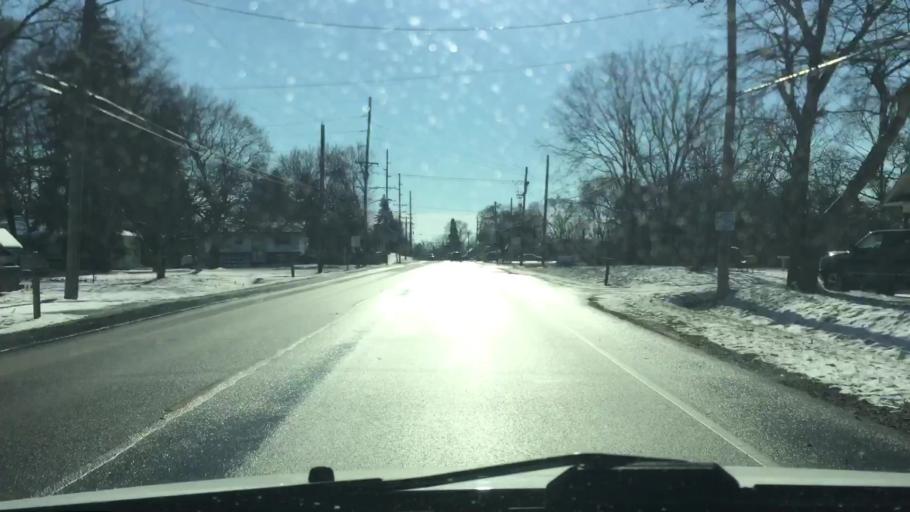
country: US
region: Illinois
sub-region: Kane County
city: Batavia
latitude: 41.8635
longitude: -88.3066
